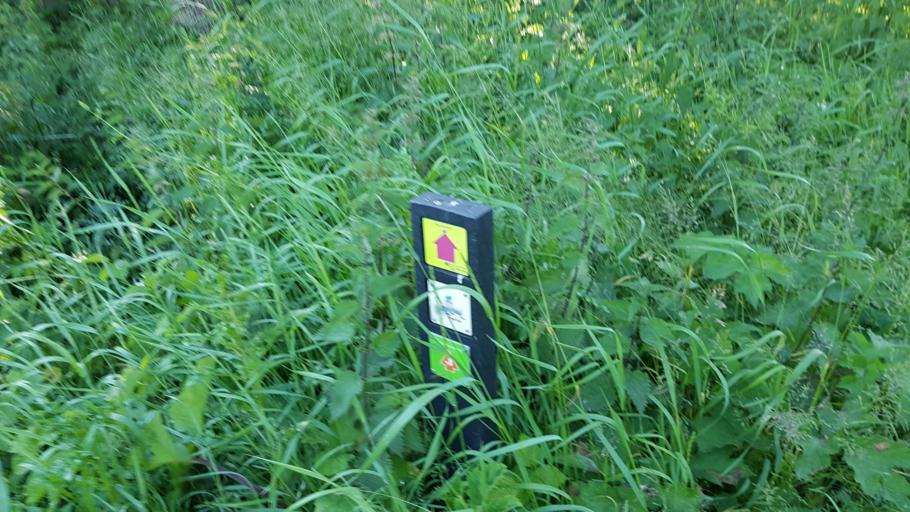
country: NL
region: South Holland
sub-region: Gemeente Noordwijkerhout
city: Noordwijkerhout
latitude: 52.2549
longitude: 4.5215
